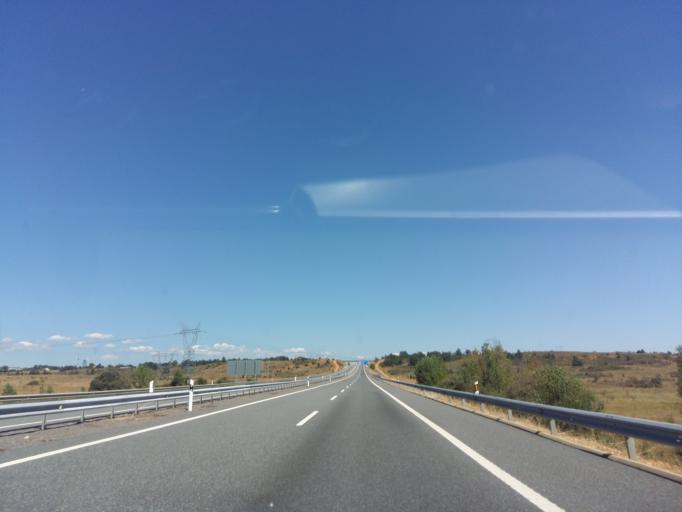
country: ES
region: Castille and Leon
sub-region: Provincia de Leon
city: Valverde de la Virgen
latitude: 42.5607
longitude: -5.6781
